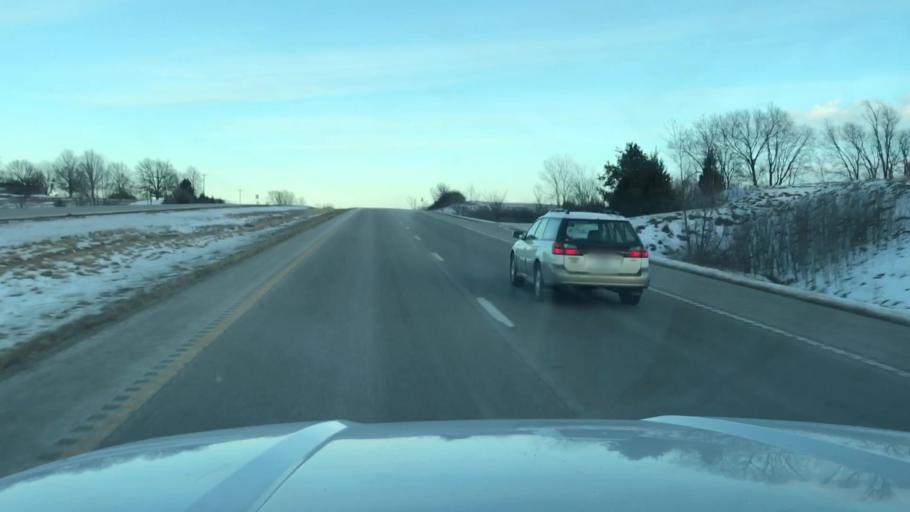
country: US
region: Missouri
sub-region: Clinton County
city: Gower
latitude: 39.7473
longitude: -94.6488
